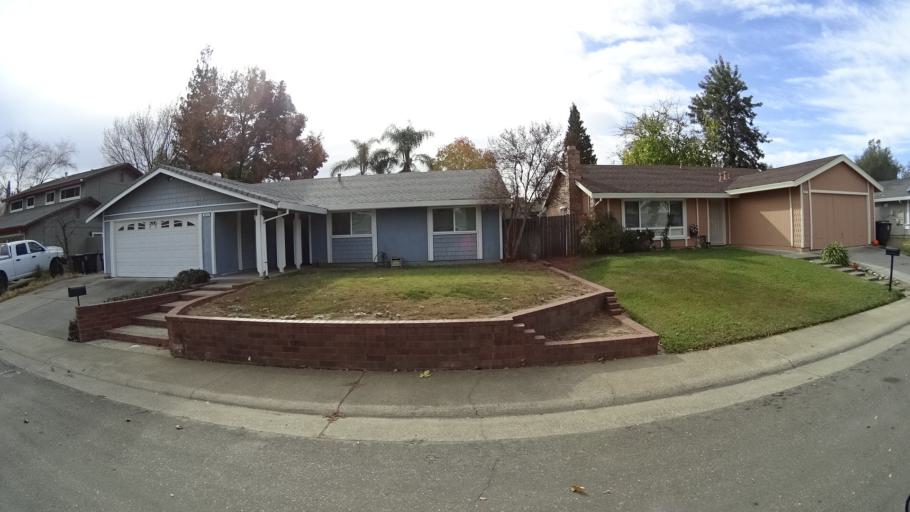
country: US
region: California
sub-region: Sacramento County
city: Citrus Heights
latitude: 38.7095
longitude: -121.2476
